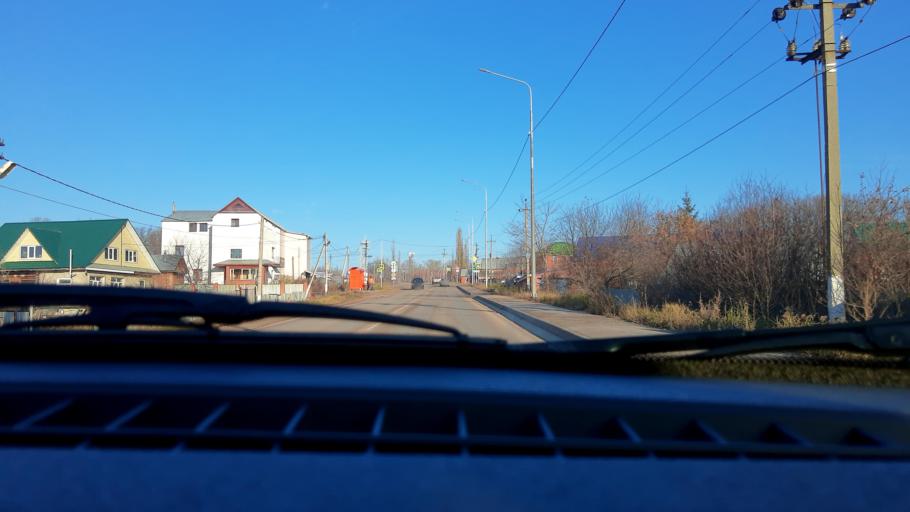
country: RU
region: Bashkortostan
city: Mikhaylovka
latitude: 54.8129
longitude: 55.8860
